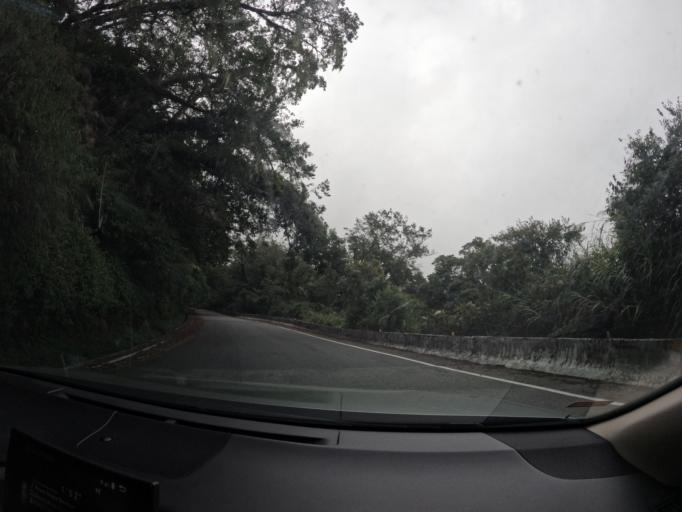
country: TW
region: Taiwan
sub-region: Taitung
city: Taitung
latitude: 23.2416
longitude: 120.9901
